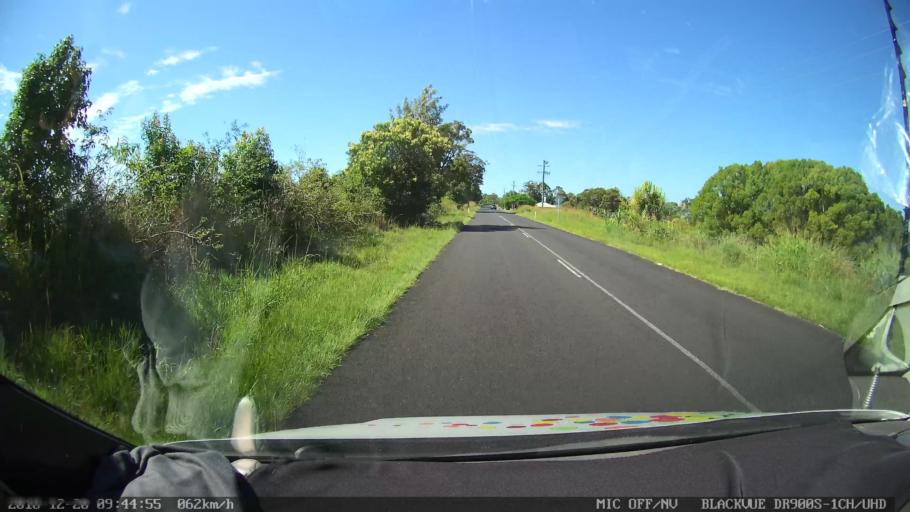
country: AU
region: New South Wales
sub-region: Lismore Municipality
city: Lismore
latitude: -28.7389
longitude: 153.2993
